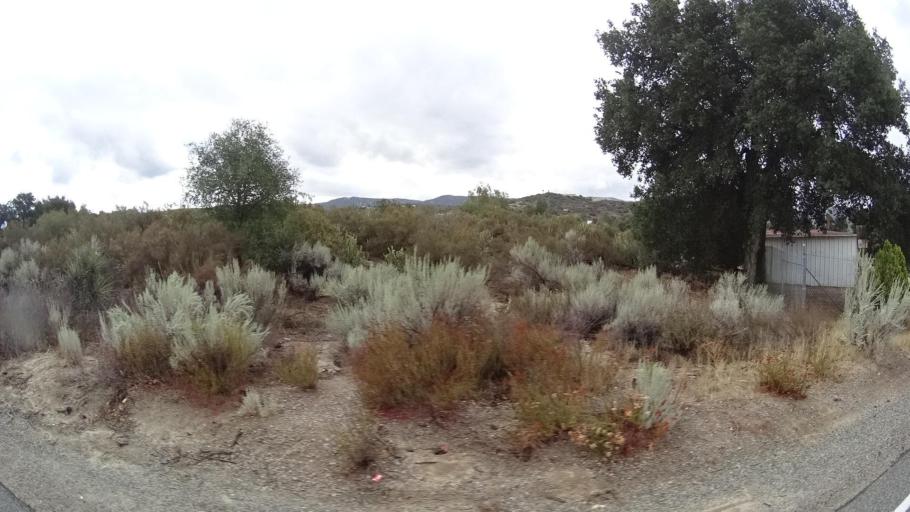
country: US
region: California
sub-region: San Diego County
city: Campo
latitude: 32.6411
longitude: -116.4288
